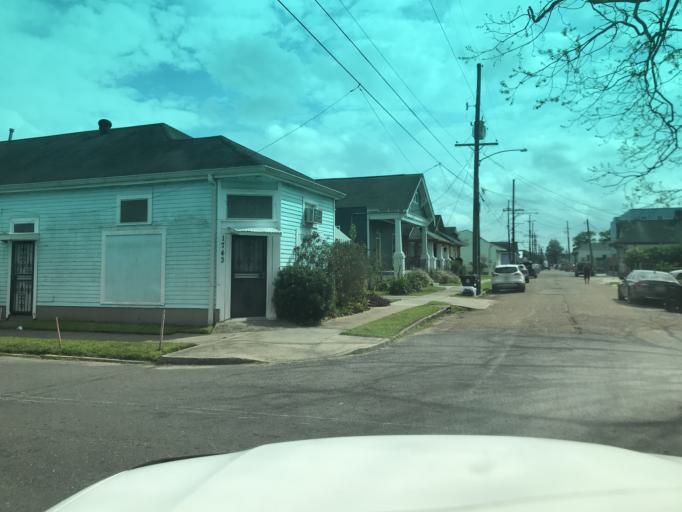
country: US
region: Louisiana
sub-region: Orleans Parish
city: New Orleans
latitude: 29.9758
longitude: -90.0562
